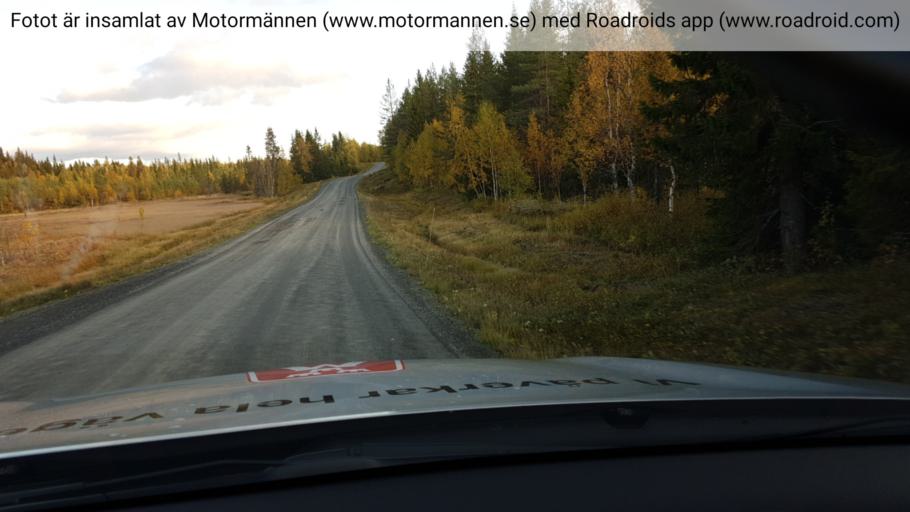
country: SE
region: Jaemtland
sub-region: Krokoms Kommun
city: Krokom
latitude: 63.7380
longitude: 14.4853
